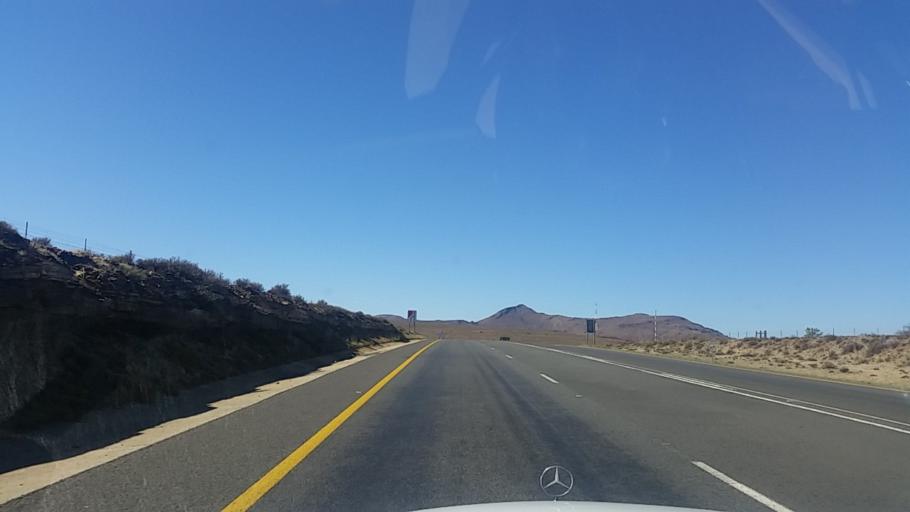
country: ZA
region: Eastern Cape
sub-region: Cacadu District Municipality
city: Graaff-Reinet
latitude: -31.9523
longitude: 24.7261
